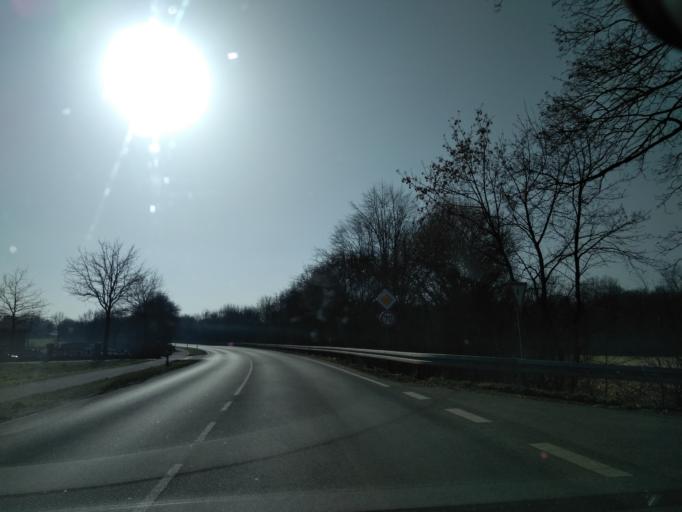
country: DE
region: North Rhine-Westphalia
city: Marl
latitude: 51.6224
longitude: 7.0488
